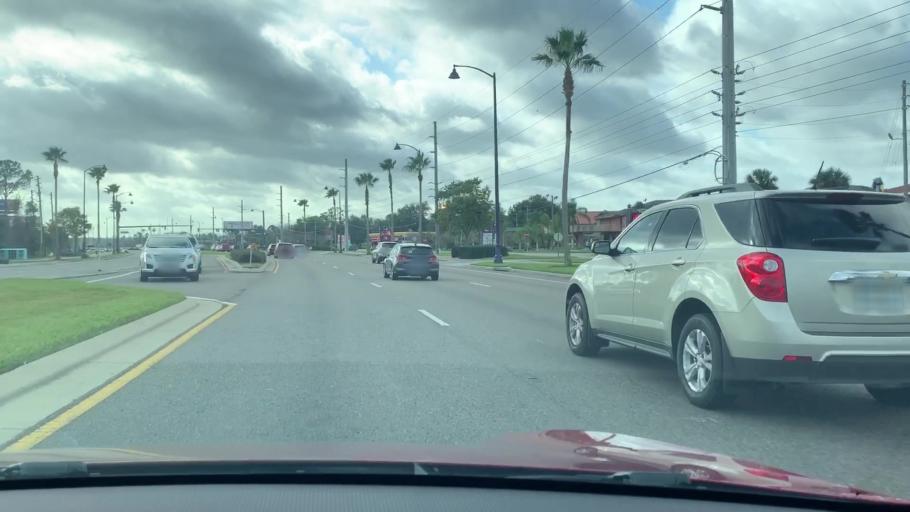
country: US
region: Florida
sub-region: Osceola County
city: Kissimmee
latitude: 28.3207
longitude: -81.4709
